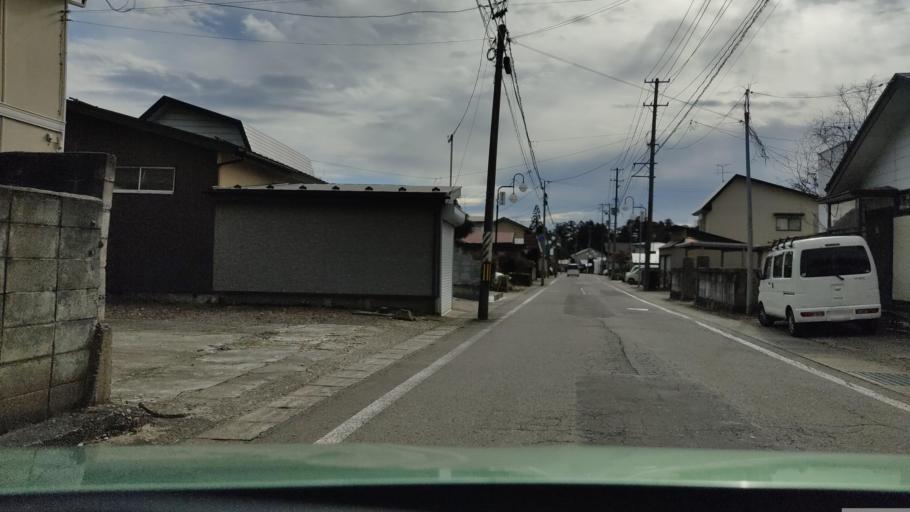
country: JP
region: Akita
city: Akita
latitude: 39.6149
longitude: 140.3223
